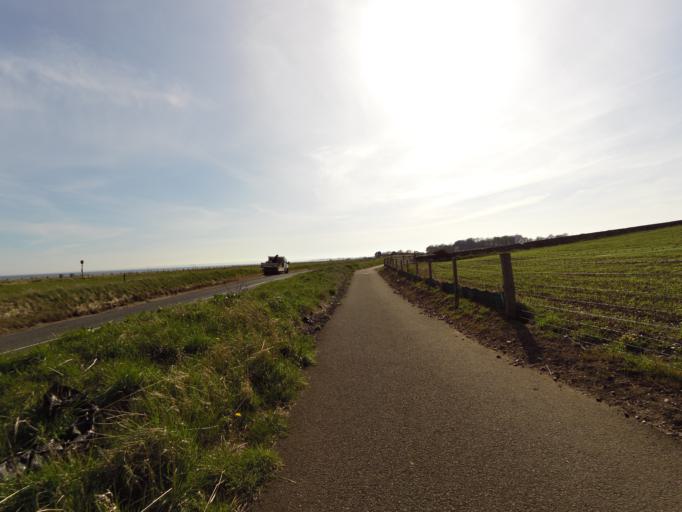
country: GB
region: Scotland
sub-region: Angus
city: Carnoustie
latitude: 56.5107
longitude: -2.6771
